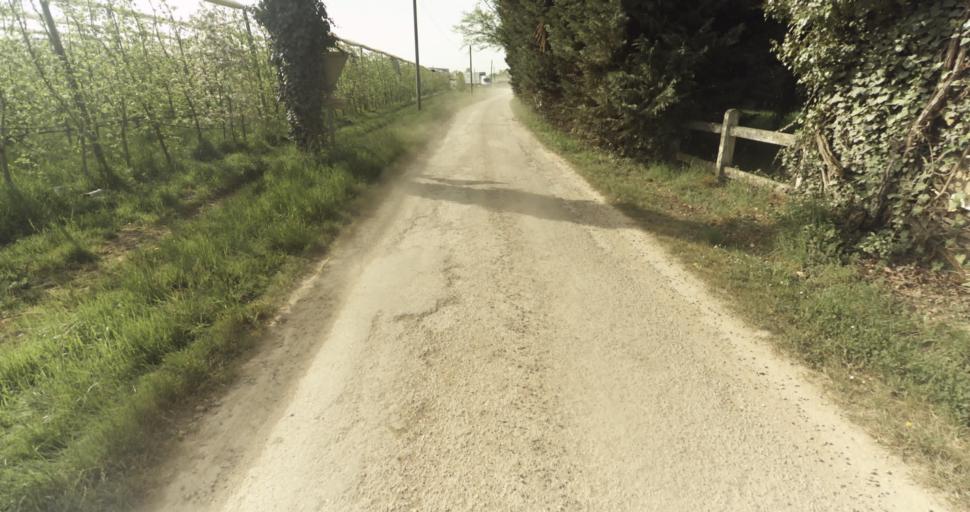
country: FR
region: Midi-Pyrenees
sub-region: Departement du Tarn-et-Garonne
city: Moissac
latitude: 44.1029
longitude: 1.1190
